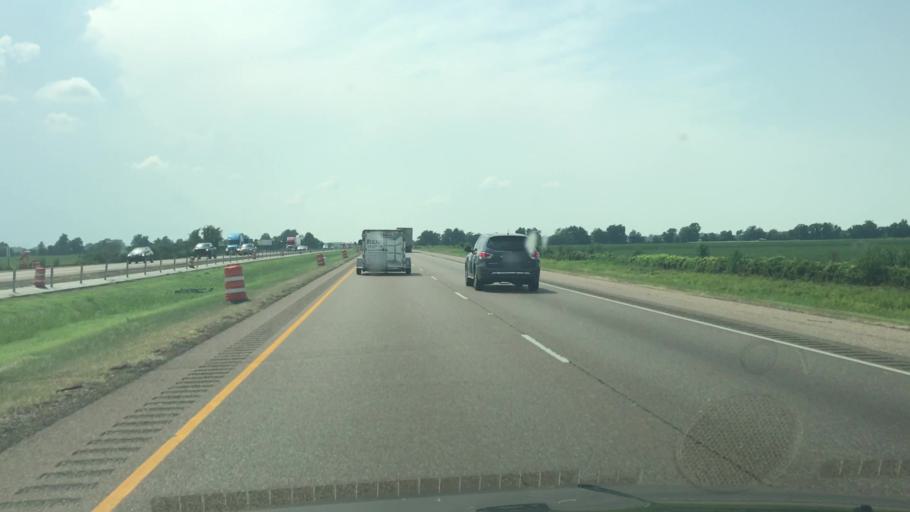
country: US
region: Arkansas
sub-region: Crittenden County
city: Earle
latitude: 35.1509
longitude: -90.3828
